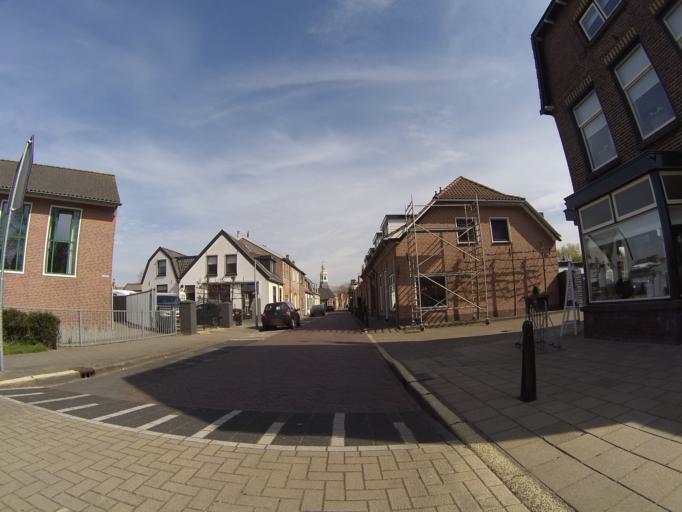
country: NL
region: Gelderland
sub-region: Gemeente Nijkerk
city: Nijkerk
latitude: 52.2198
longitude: 5.4809
